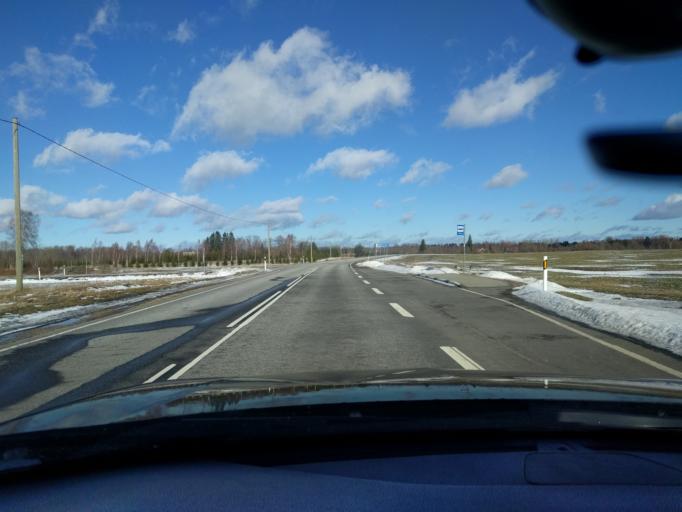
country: EE
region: Harju
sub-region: Raasiku vald
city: Raasiku
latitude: 59.3527
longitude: 25.1458
